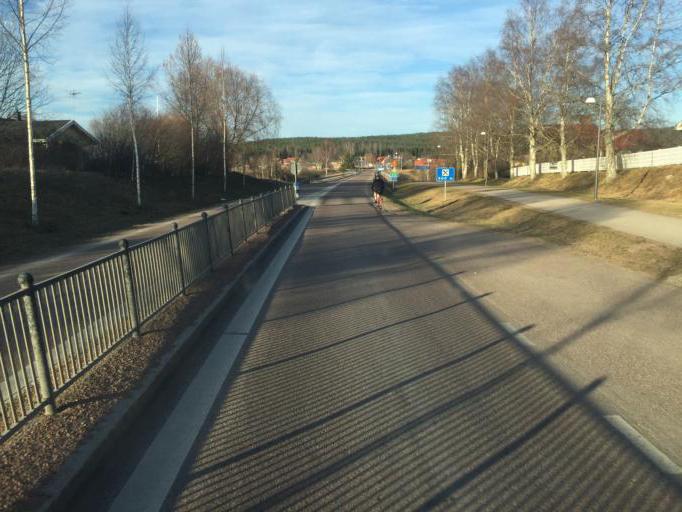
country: SE
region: Dalarna
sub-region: Gagnefs Kommun
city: Djuras
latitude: 60.5574
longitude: 15.1221
